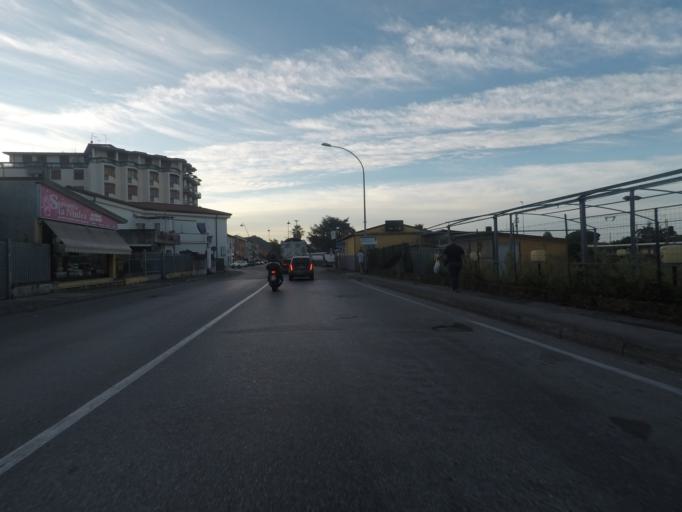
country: IT
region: Tuscany
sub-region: Provincia di Massa-Carrara
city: Massa
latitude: 44.0252
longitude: 10.1357
